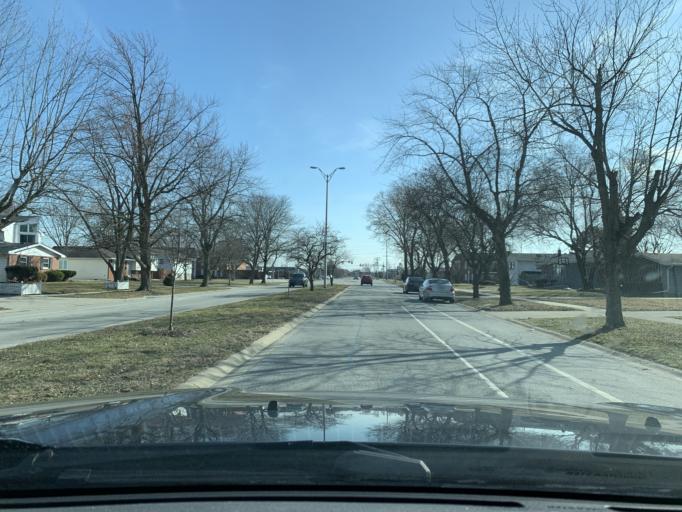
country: US
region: Indiana
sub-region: Lake County
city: Highland
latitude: 41.5394
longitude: -87.4855
